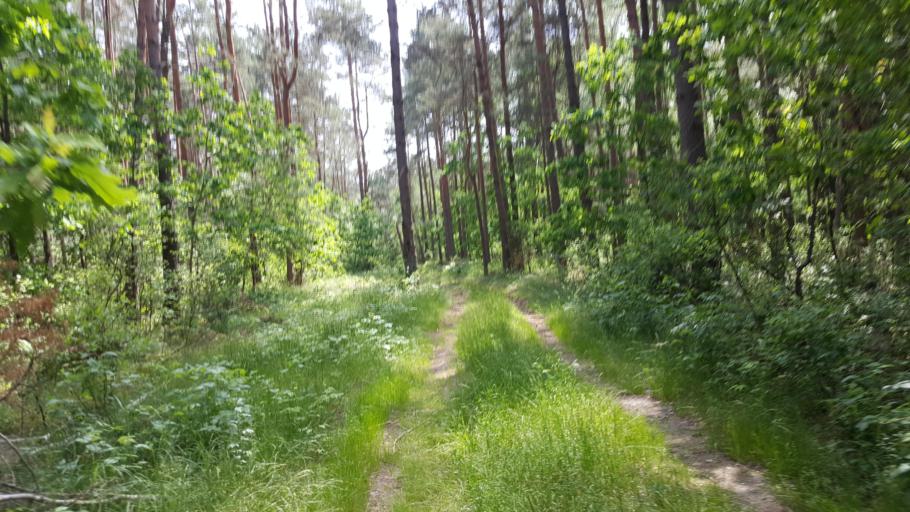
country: BY
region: Brest
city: Kamyanyuki
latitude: 52.5118
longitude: 23.8270
